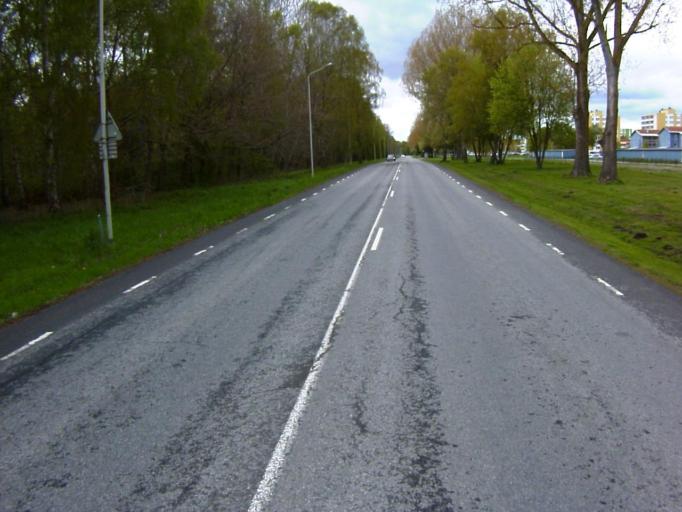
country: SE
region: Skane
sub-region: Kristianstads Kommun
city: Kristianstad
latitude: 56.0393
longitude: 14.1869
